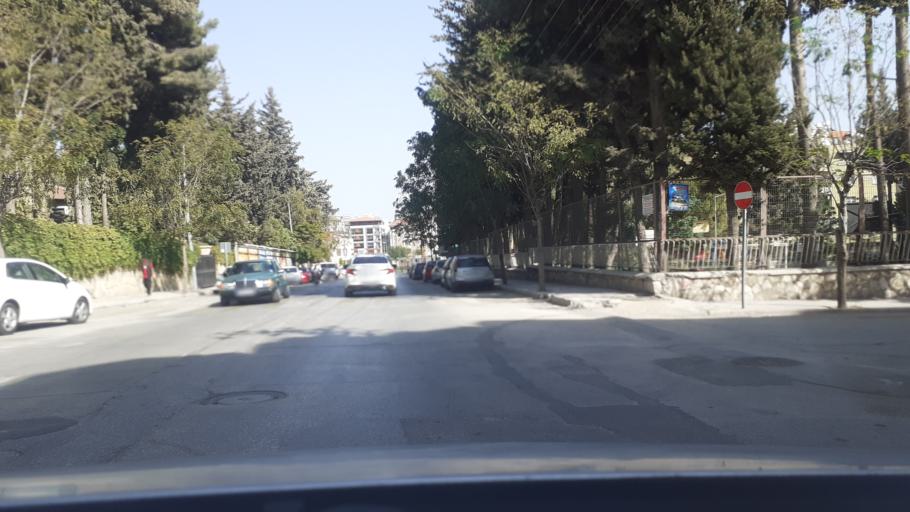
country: TR
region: Hatay
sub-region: Antakya Ilcesi
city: Antakya
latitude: 36.2117
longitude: 36.1553
